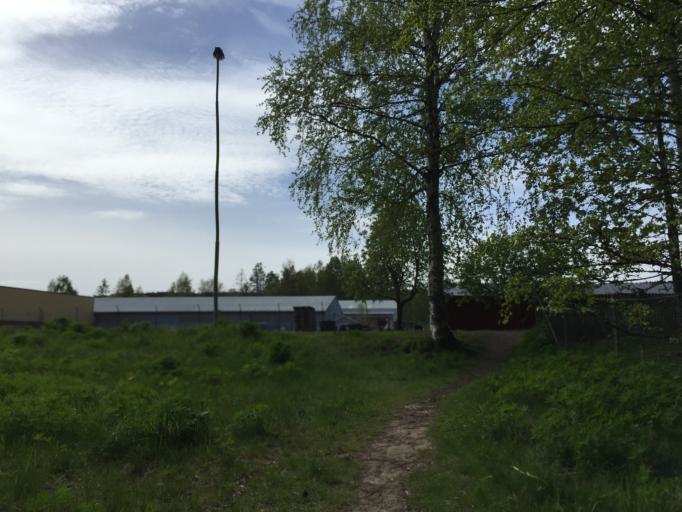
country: SE
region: Dalarna
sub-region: Ludvika Kommun
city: Ludvika
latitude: 60.1369
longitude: 15.1665
